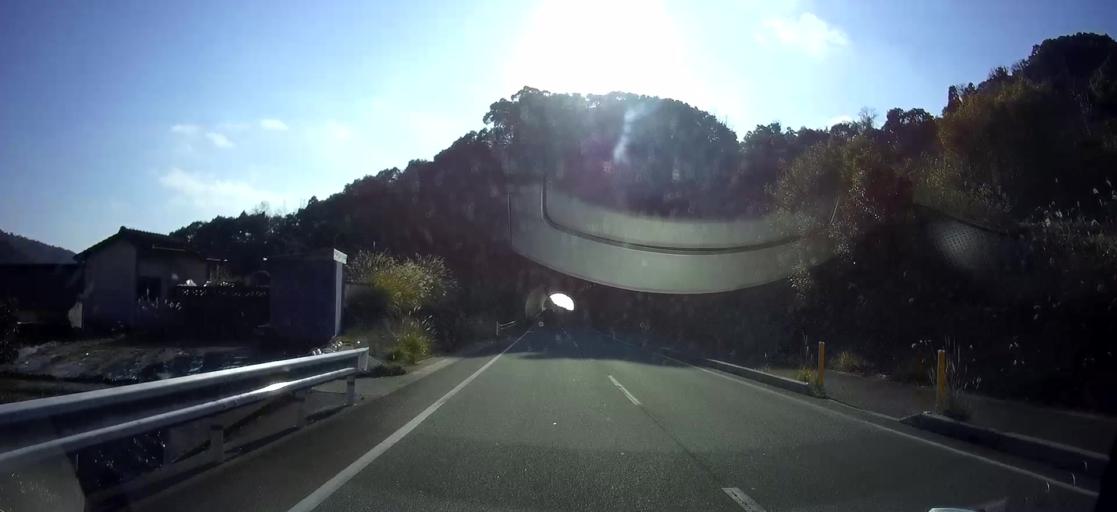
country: JP
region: Kumamoto
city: Minamata
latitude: 32.3984
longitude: 130.3982
